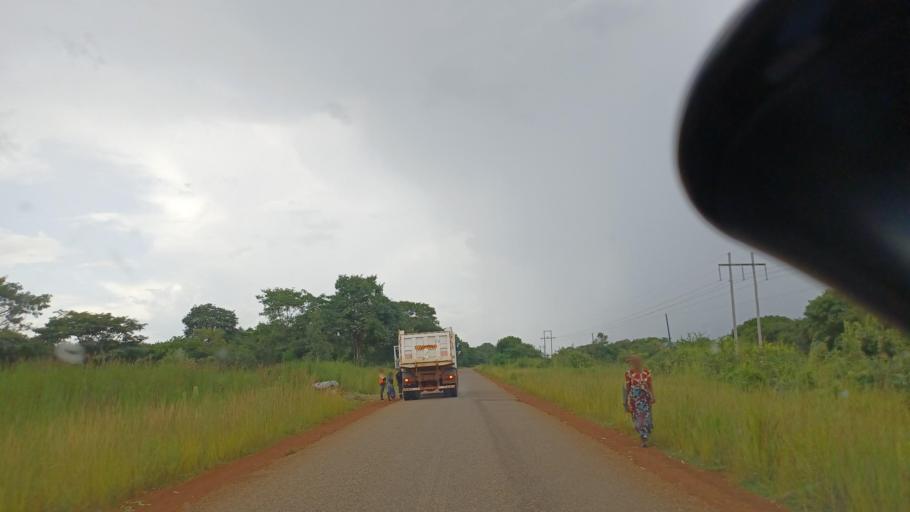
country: ZM
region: North-Western
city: Kasempa
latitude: -13.0440
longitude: 25.9922
